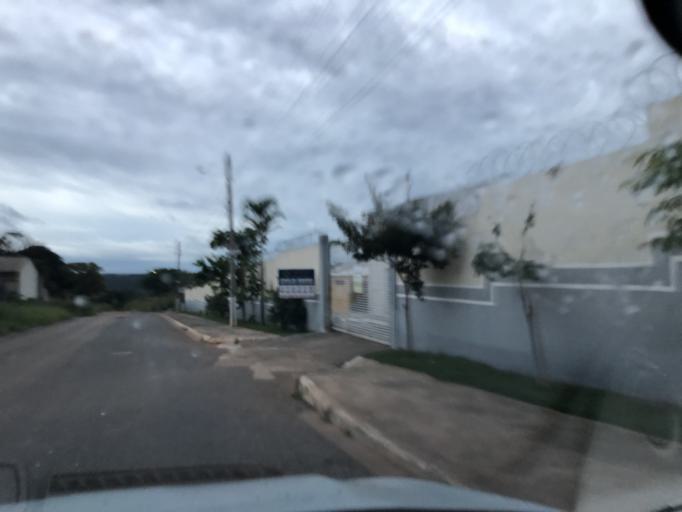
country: BR
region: Goias
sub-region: Luziania
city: Luziania
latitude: -16.1151
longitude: -47.9865
